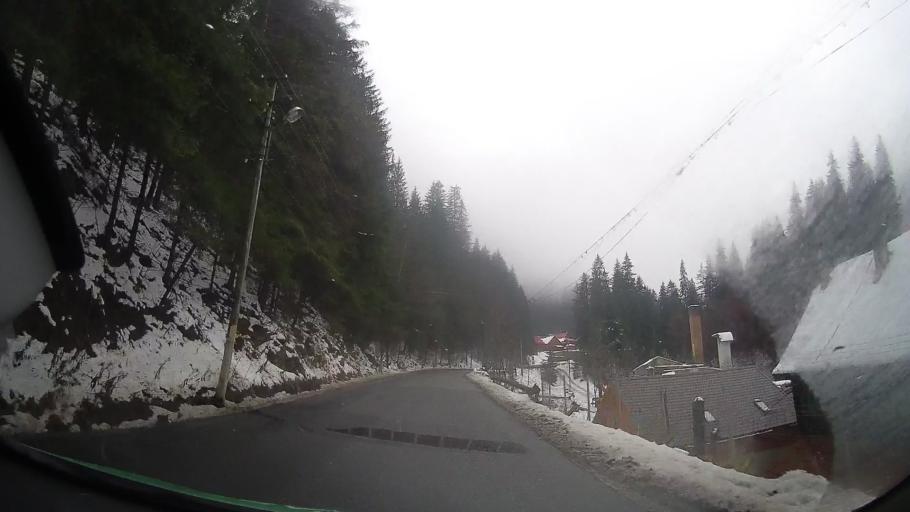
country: RO
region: Neamt
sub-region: Comuna Bicaz Chei
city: Bicaz Chei
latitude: 46.7945
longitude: 25.8007
